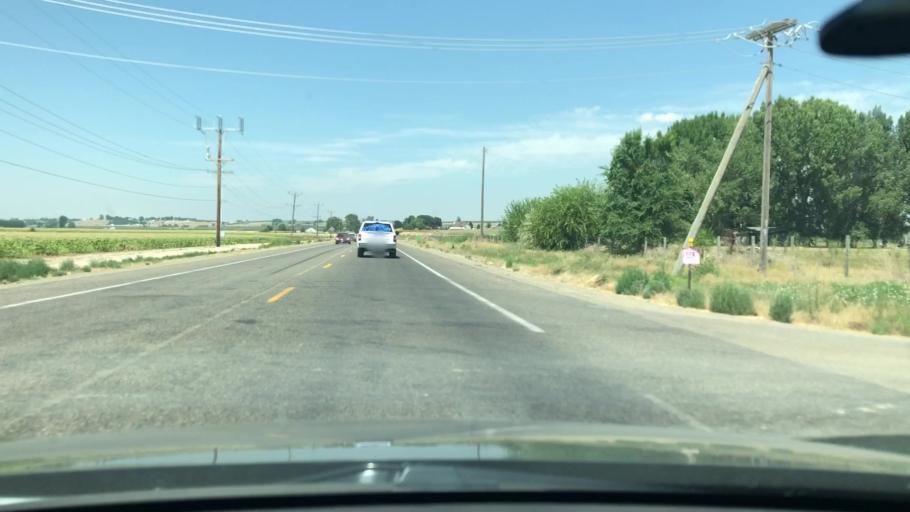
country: US
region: Idaho
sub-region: Owyhee County
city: Homedale
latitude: 43.6323
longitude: -116.9120
